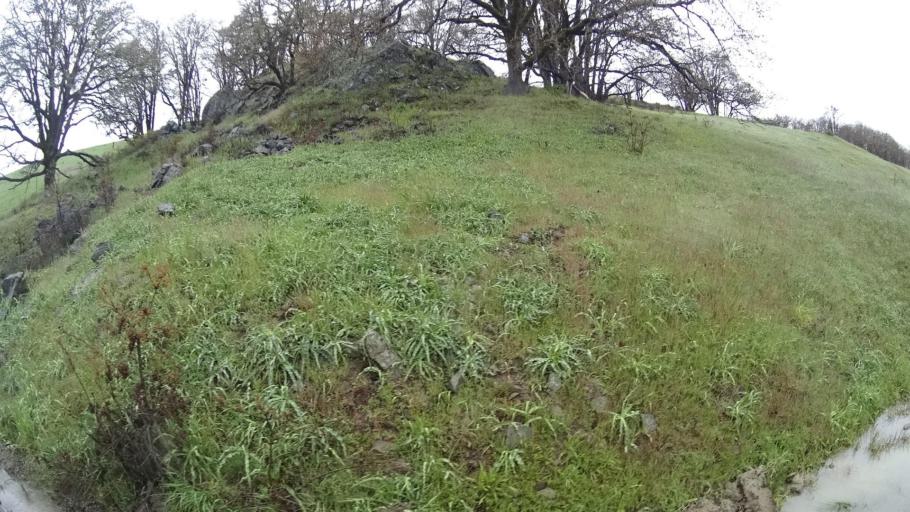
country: US
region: California
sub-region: Humboldt County
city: Westhaven-Moonstone
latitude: 41.1465
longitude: -123.8868
